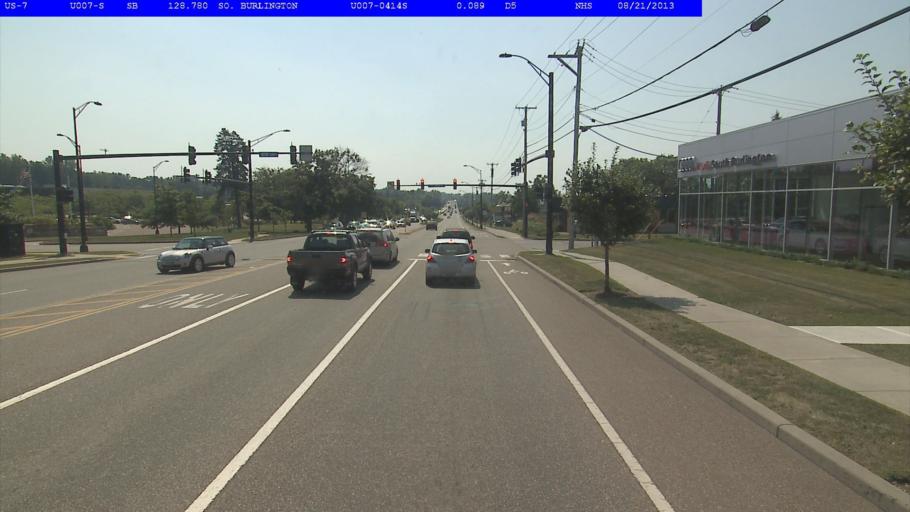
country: US
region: Vermont
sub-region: Chittenden County
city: Burlington
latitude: 44.4337
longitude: -73.2109
